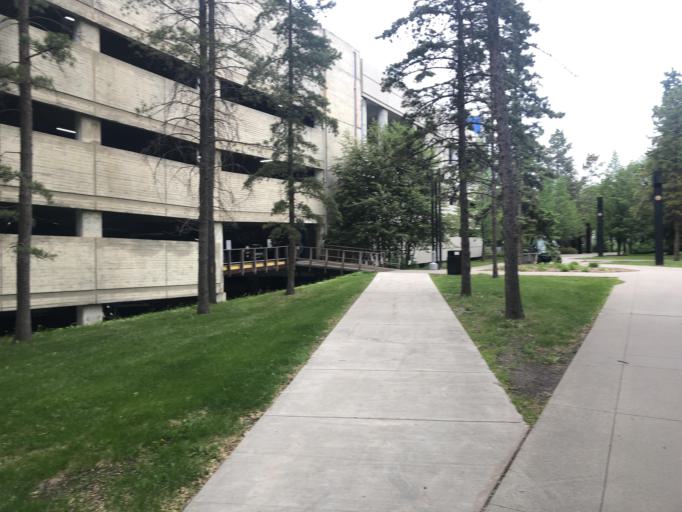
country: CA
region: Alberta
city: Edmonton
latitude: 53.5287
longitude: -113.5287
